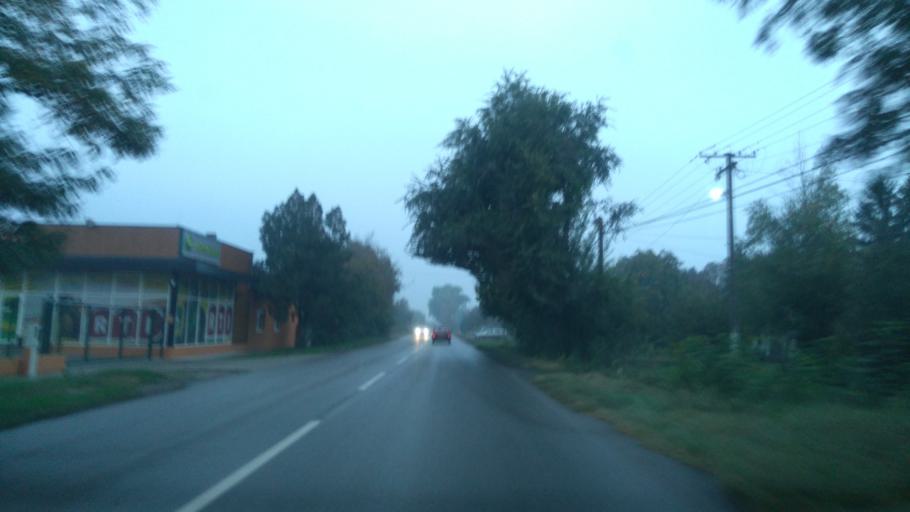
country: RS
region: Autonomna Pokrajina Vojvodina
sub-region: Juznobacki Okrug
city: Becej
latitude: 45.6314
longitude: 20.0332
